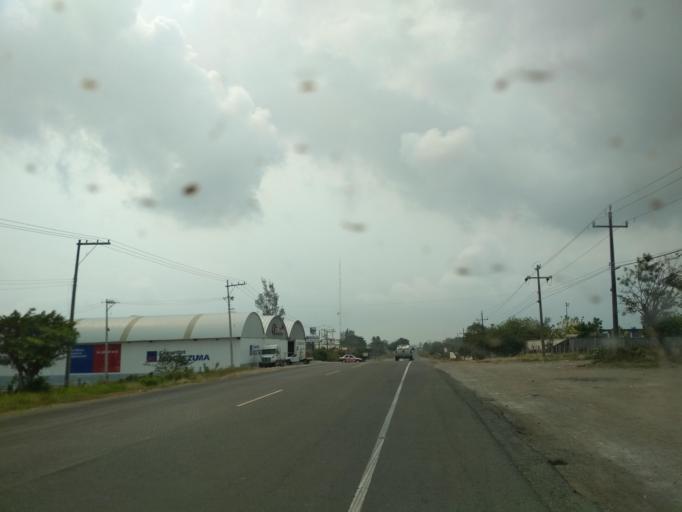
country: MX
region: Veracruz
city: Paso del Toro
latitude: 19.0097
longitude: -96.1175
